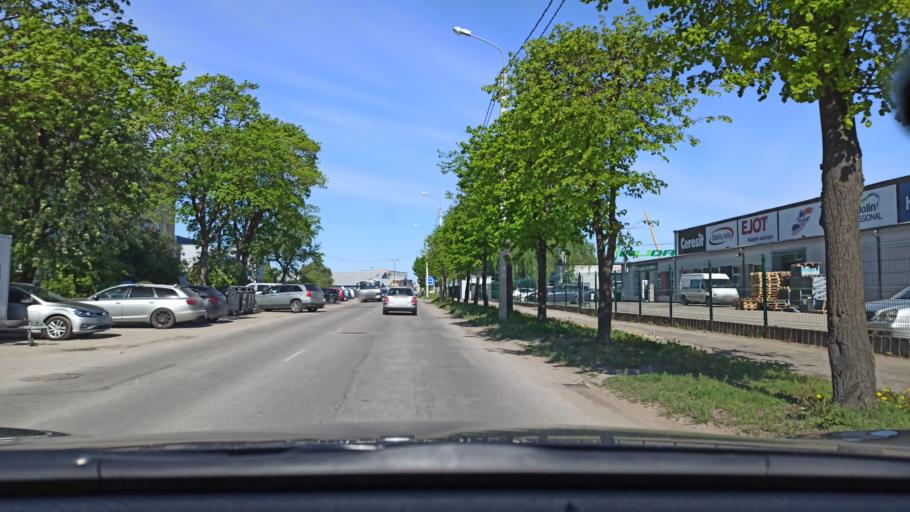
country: LT
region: Siauliu apskritis
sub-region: Siauliai
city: Siauliai
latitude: 55.9497
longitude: 23.3091
